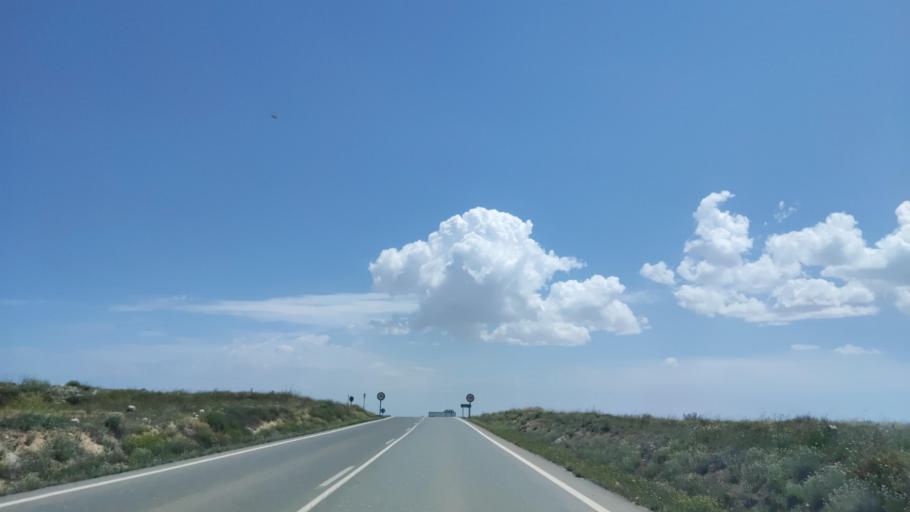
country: ES
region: Castille-La Mancha
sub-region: Province of Toledo
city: Mascaraque
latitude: 39.7158
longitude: -3.8227
